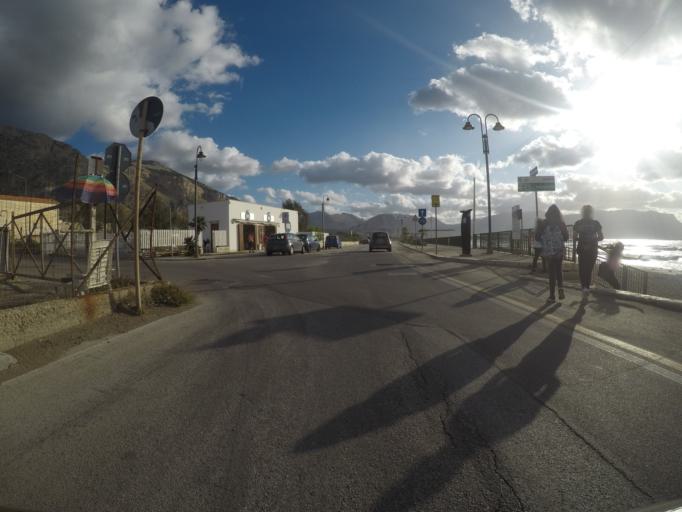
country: IT
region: Sicily
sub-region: Palermo
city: Isola delle Femmine
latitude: 38.1924
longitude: 13.2442
